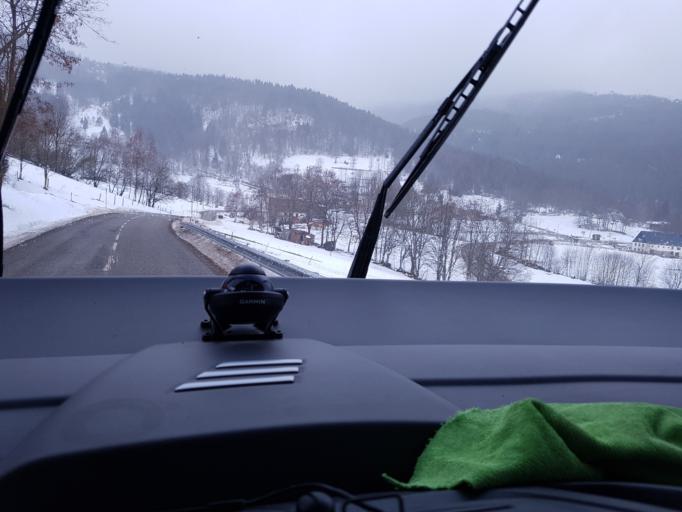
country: FR
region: Alsace
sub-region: Departement du Haut-Rhin
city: Soultzeren
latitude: 48.1086
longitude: 7.1162
